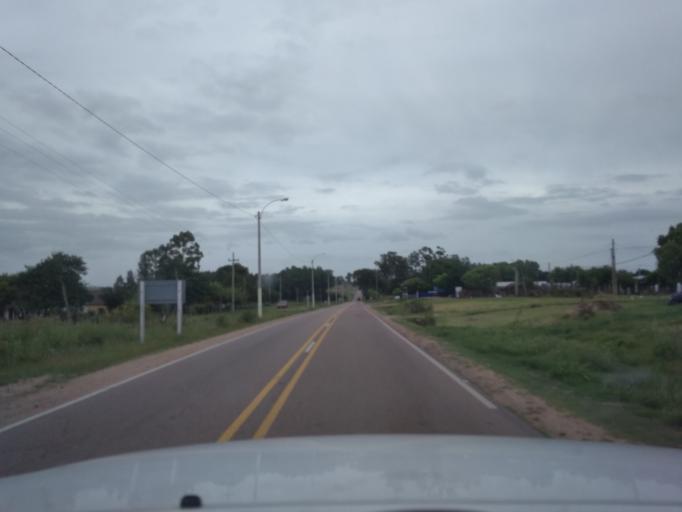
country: UY
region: Canelones
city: Tala
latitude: -34.3522
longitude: -55.7689
